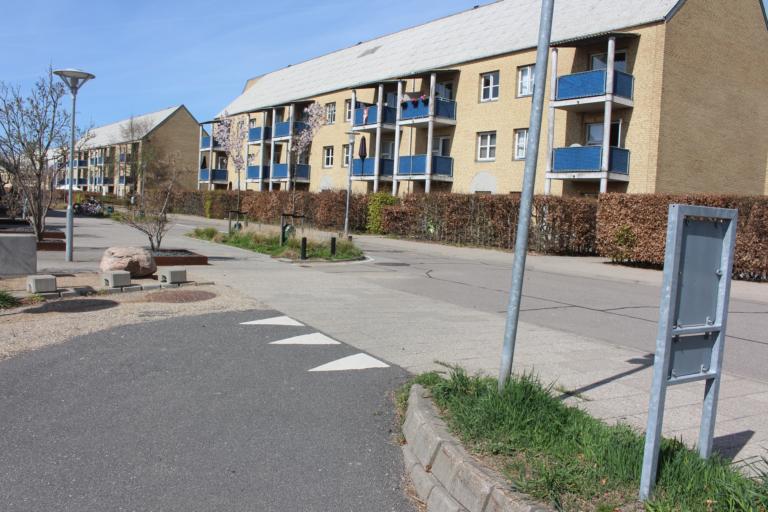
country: DK
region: Capital Region
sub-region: Glostrup Kommune
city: Glostrup
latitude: 55.6831
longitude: 12.4190
